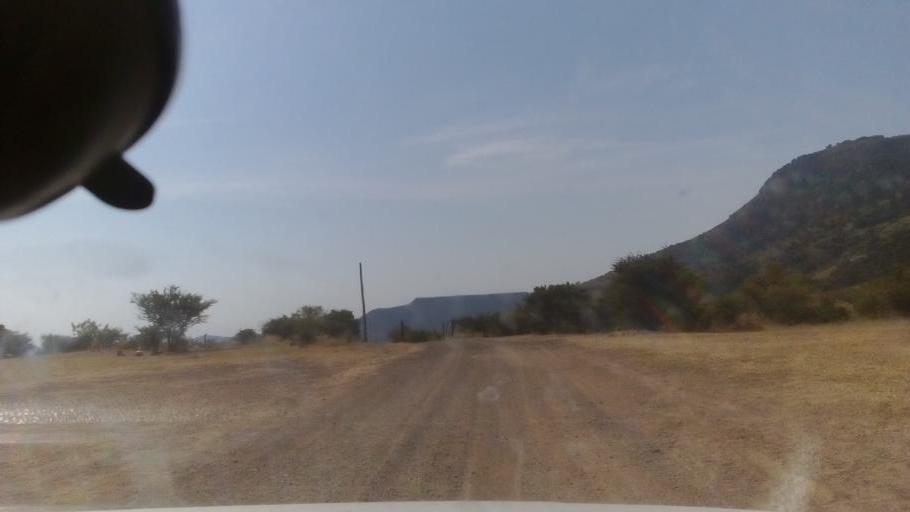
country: MX
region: Guanajuato
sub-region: Leon
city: Lucio Blanco (Los Gavilanes)
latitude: 21.1999
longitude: -101.4989
